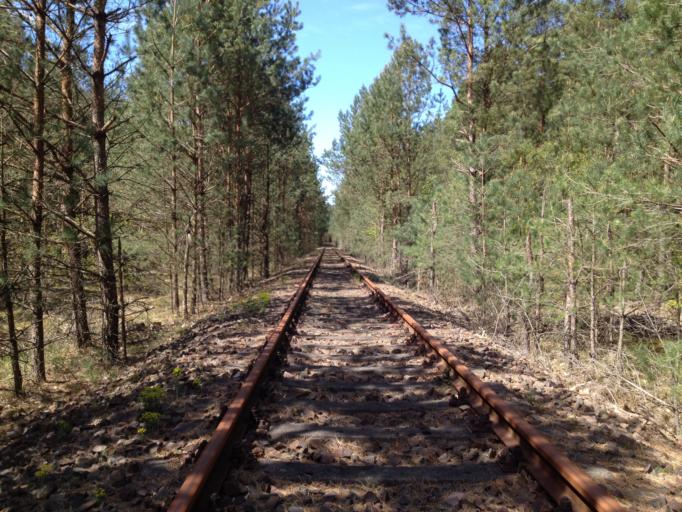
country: DE
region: Brandenburg
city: Lychen
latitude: 53.1701
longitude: 13.3621
